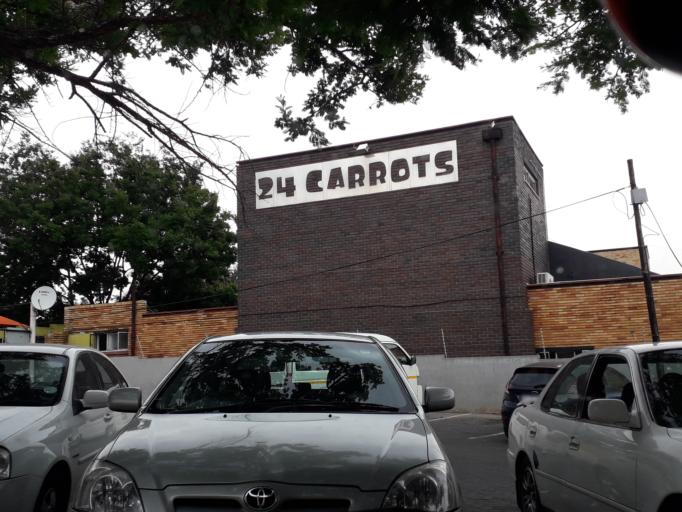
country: ZA
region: Gauteng
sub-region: City of Johannesburg Metropolitan Municipality
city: Johannesburg
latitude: -26.1577
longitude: 28.0846
